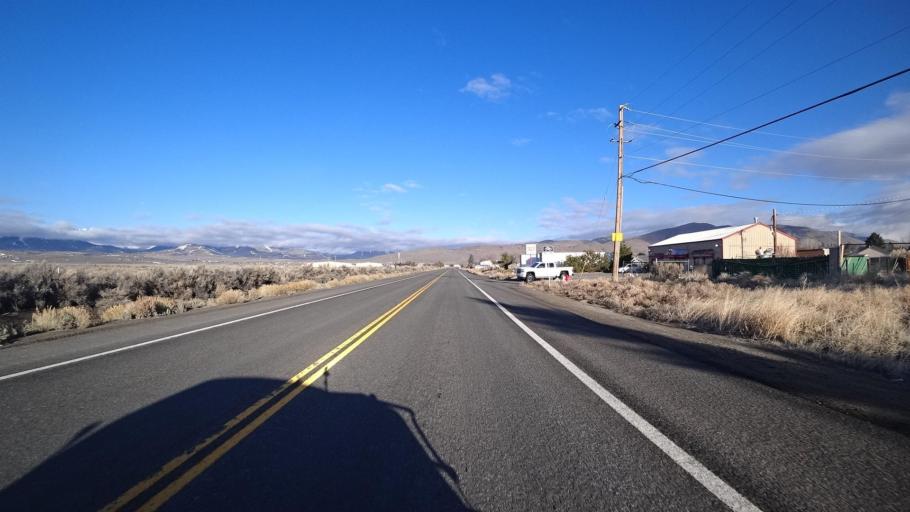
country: US
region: Nevada
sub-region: Washoe County
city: Cold Springs
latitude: 39.6713
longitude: -119.9656
